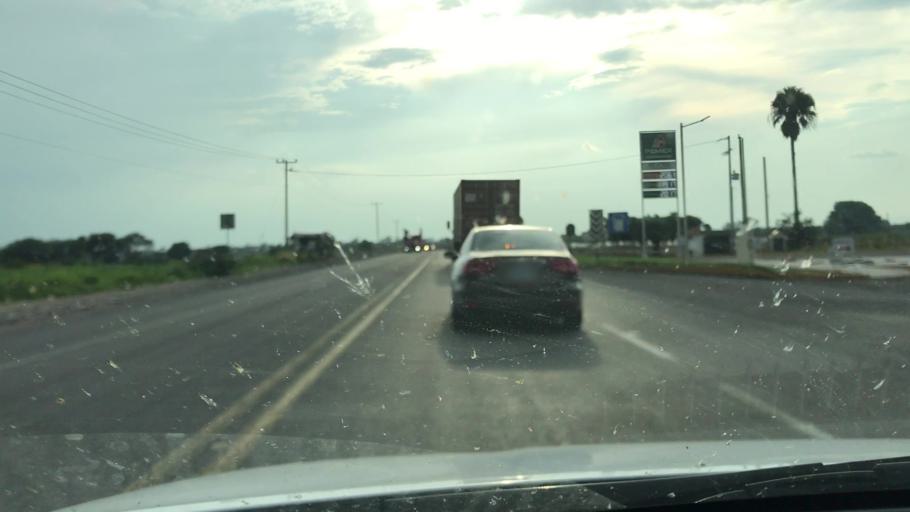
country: MX
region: Michoacan
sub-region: Yurecuaro
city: Yurecuaro
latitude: 20.3283
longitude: -102.2626
